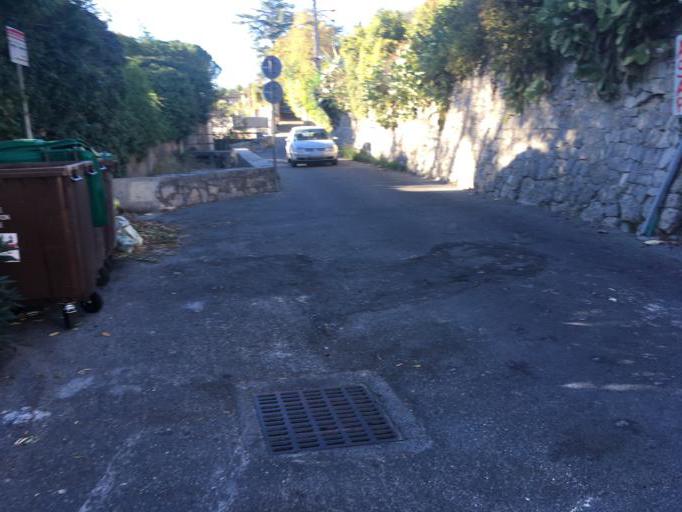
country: FR
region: Provence-Alpes-Cote d'Azur
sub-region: Departement du Var
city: Draguignan
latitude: 43.5430
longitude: 6.4628
